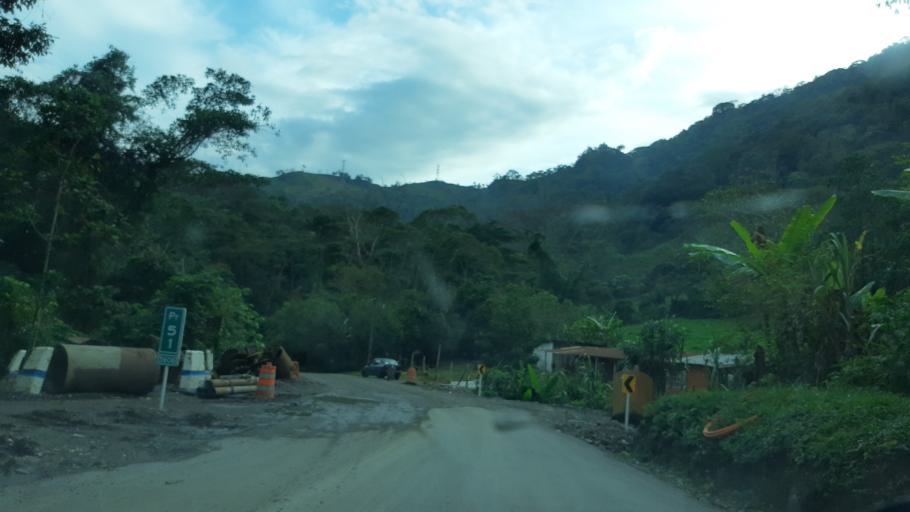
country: CO
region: Boyaca
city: Santa Maria
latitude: 4.8755
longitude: -73.2464
